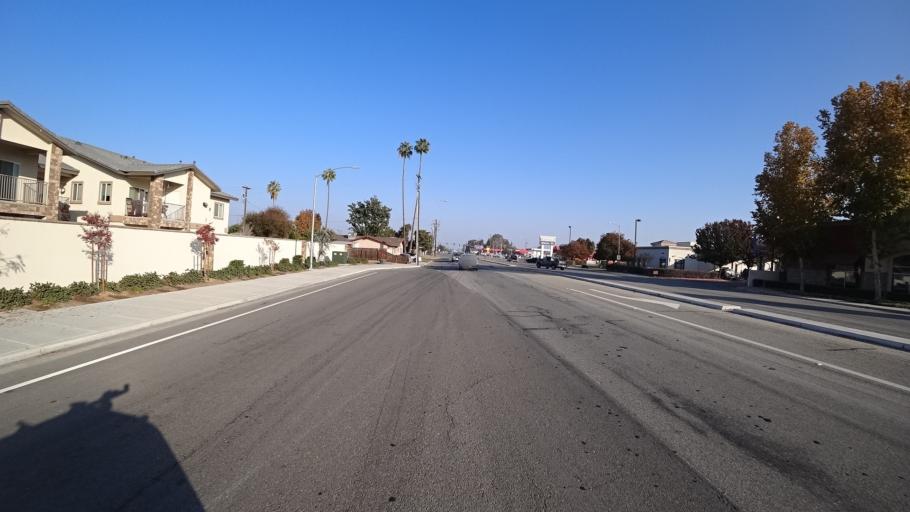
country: US
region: California
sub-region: Kern County
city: Rosedale
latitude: 35.3836
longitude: -119.1482
